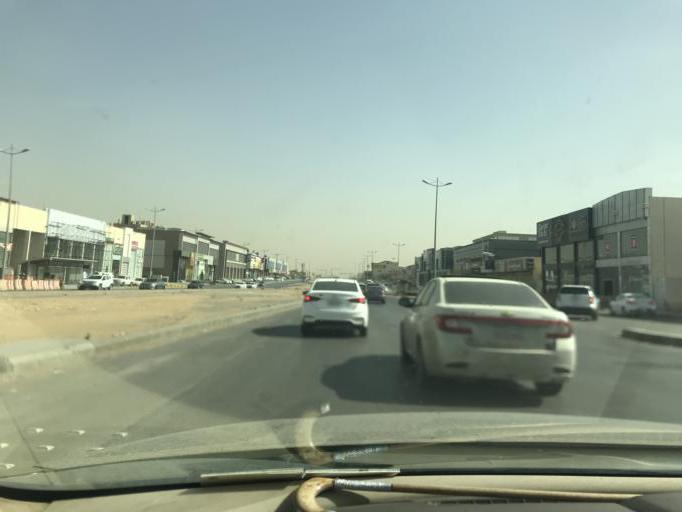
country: SA
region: Ar Riyad
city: Riyadh
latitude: 24.8047
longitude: 46.7379
